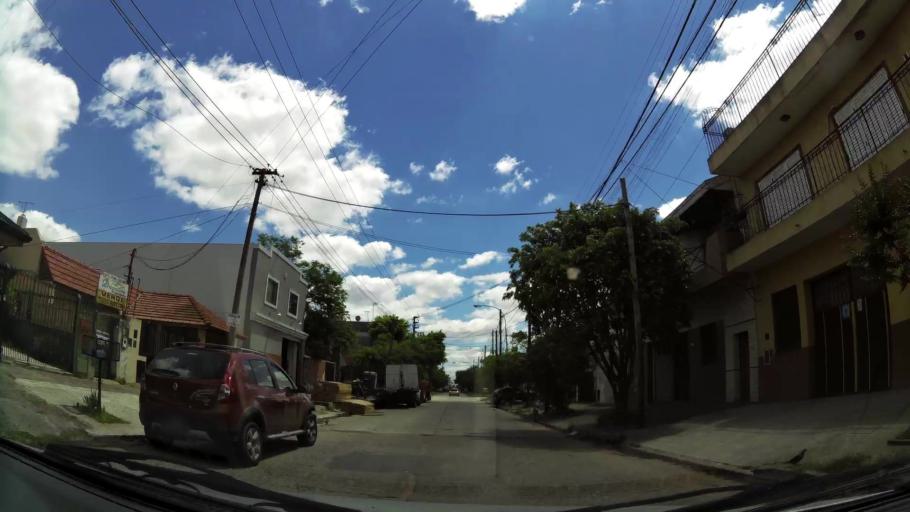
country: AR
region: Buenos Aires
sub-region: Partido de Lanus
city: Lanus
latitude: -34.7140
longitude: -58.4226
